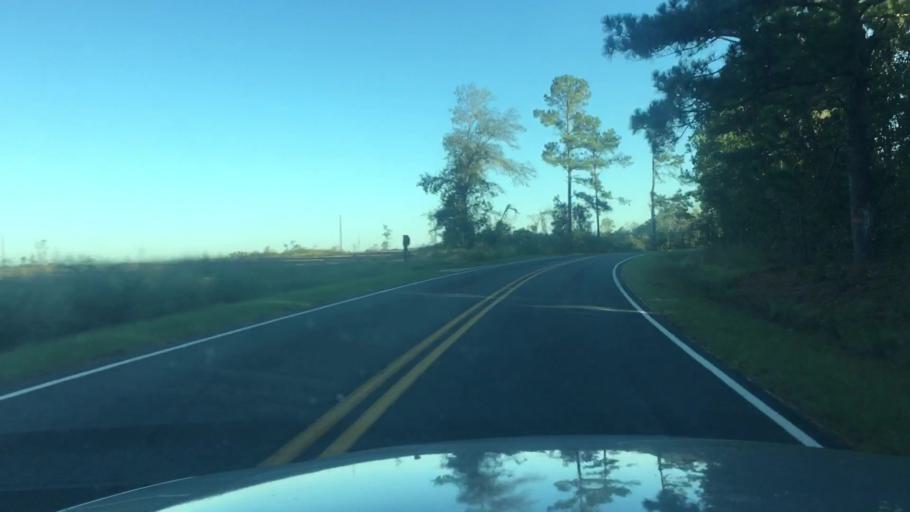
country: US
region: North Carolina
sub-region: Harnett County
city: Walkertown
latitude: 35.2846
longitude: -78.8692
